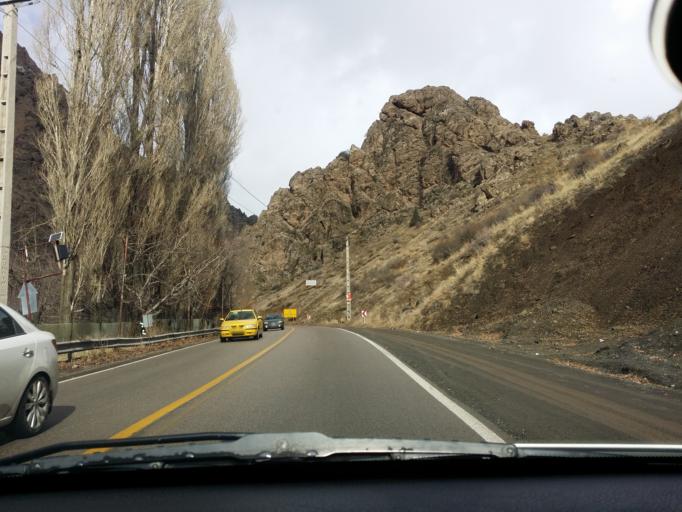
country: IR
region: Tehran
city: Tajrish
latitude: 36.0423
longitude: 51.3114
